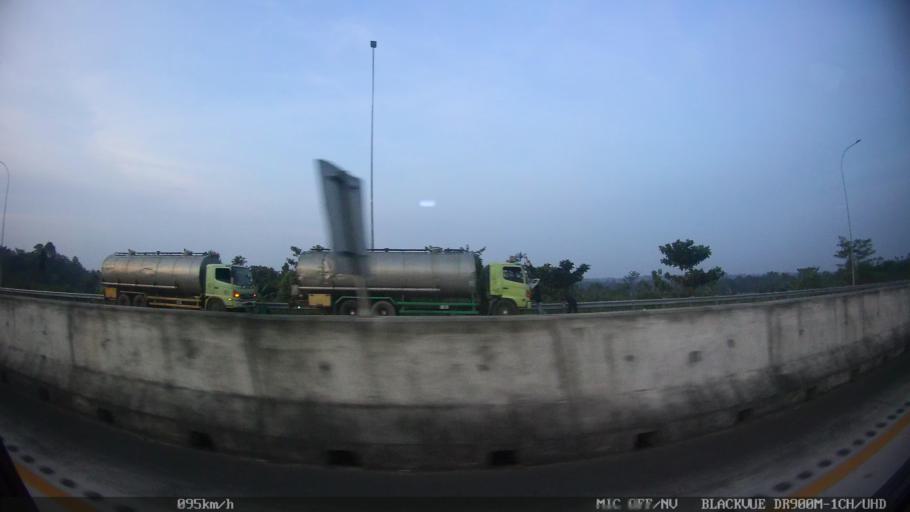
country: ID
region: Lampung
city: Pasuruan
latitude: -5.7298
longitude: 105.6733
